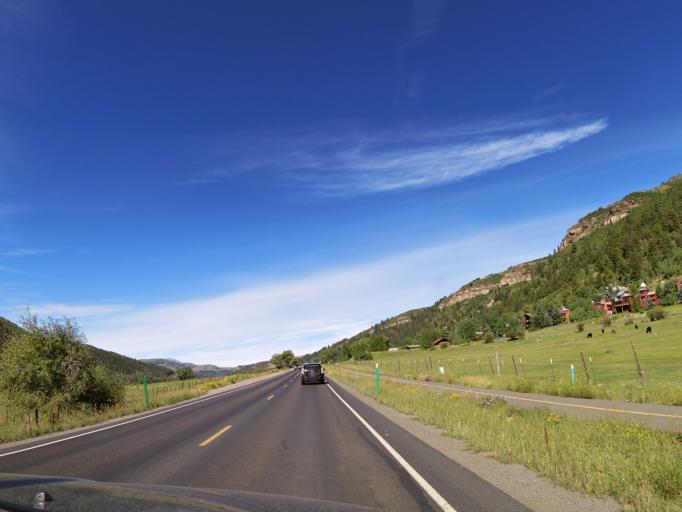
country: US
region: Colorado
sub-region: San Miguel County
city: Mountain Village
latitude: 37.9479
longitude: -107.8445
